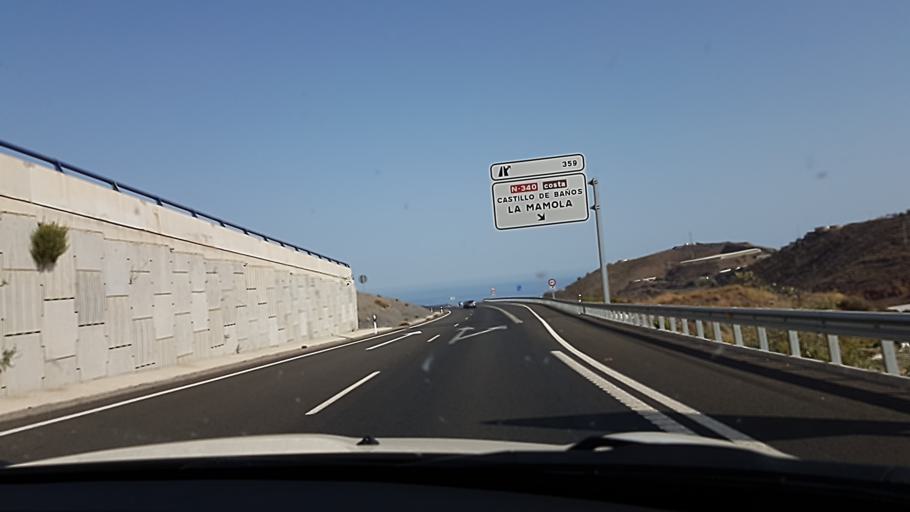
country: ES
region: Andalusia
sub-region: Provincia de Granada
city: Polopos
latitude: 36.7506
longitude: -3.3185
